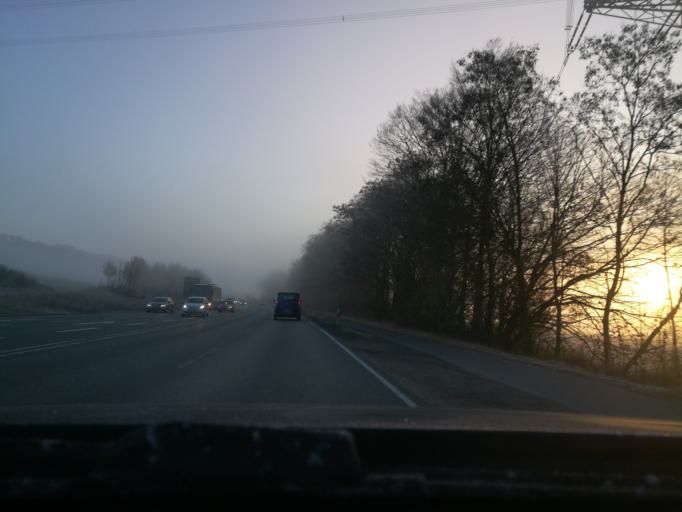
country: DE
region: Bavaria
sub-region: Regierungsbezirk Mittelfranken
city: Obermichelbach
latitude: 49.5639
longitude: 10.9350
